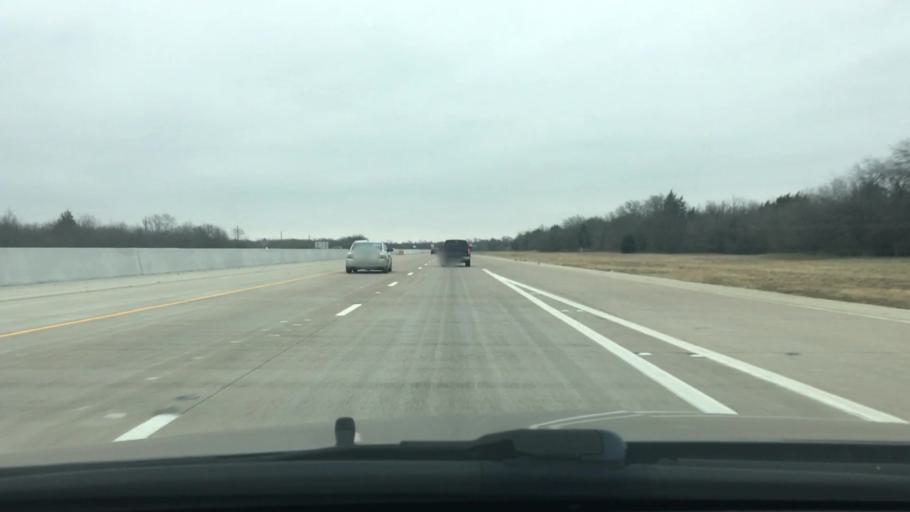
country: US
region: Texas
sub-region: Freestone County
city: Wortham
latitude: 31.8761
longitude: -96.3420
